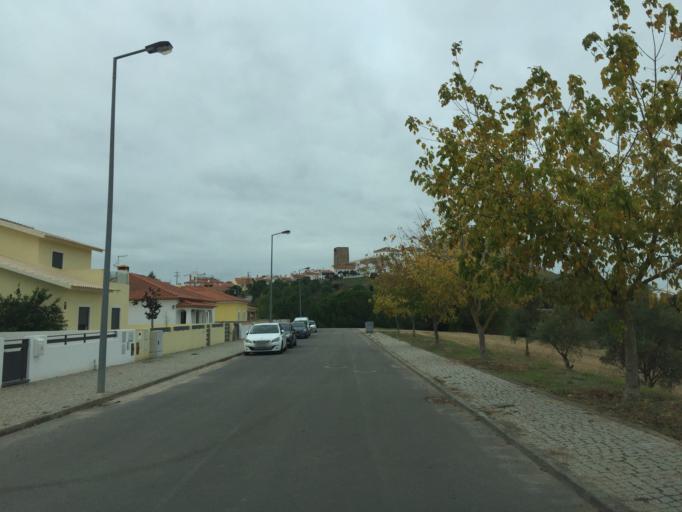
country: PT
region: Portalegre
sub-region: Avis
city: Avis
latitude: 39.0535
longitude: -7.8855
